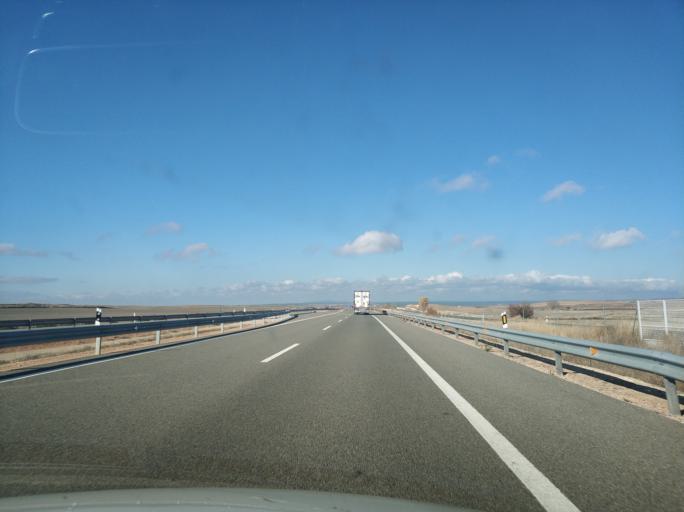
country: ES
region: Castille and Leon
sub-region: Provincia de Soria
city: Coscurita
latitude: 41.4035
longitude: -2.4791
